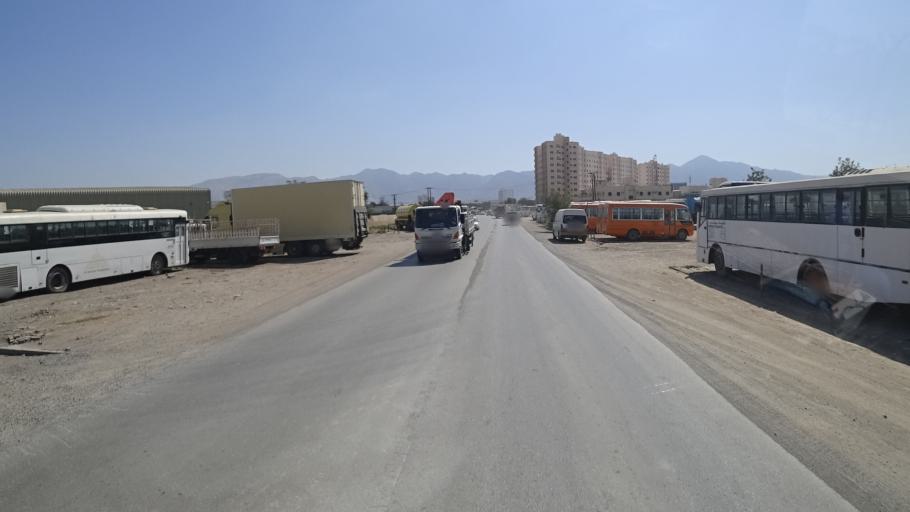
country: OM
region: Muhafazat Masqat
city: Bawshar
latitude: 23.5786
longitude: 58.3652
